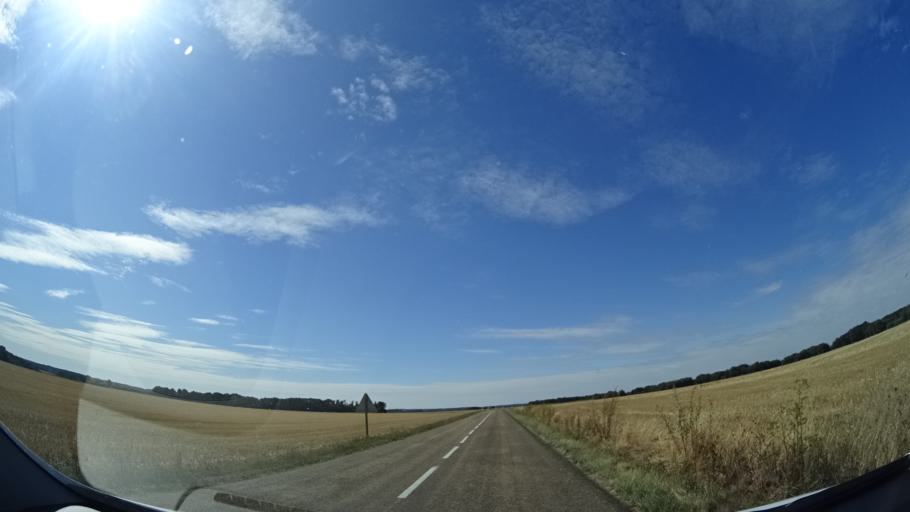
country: FR
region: Bourgogne
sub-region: Departement de l'Yonne
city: Cezy
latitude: 47.9320
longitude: 3.2684
